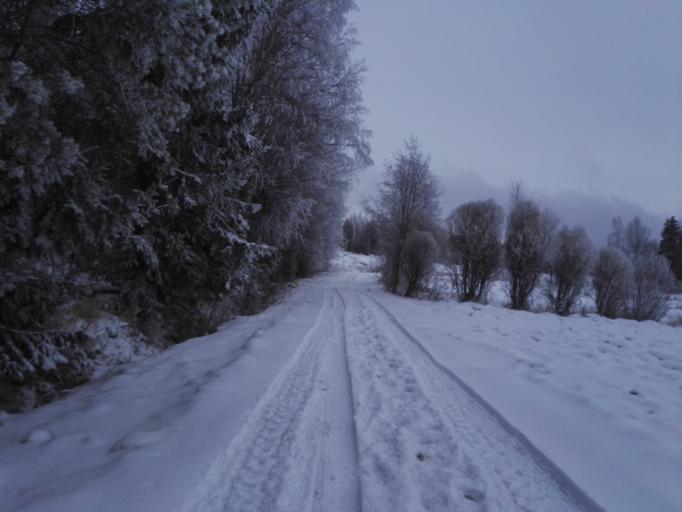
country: FI
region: Satakunta
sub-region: Pohjois-Satakunta
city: Jaemijaervi
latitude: 61.7839
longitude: 22.8758
